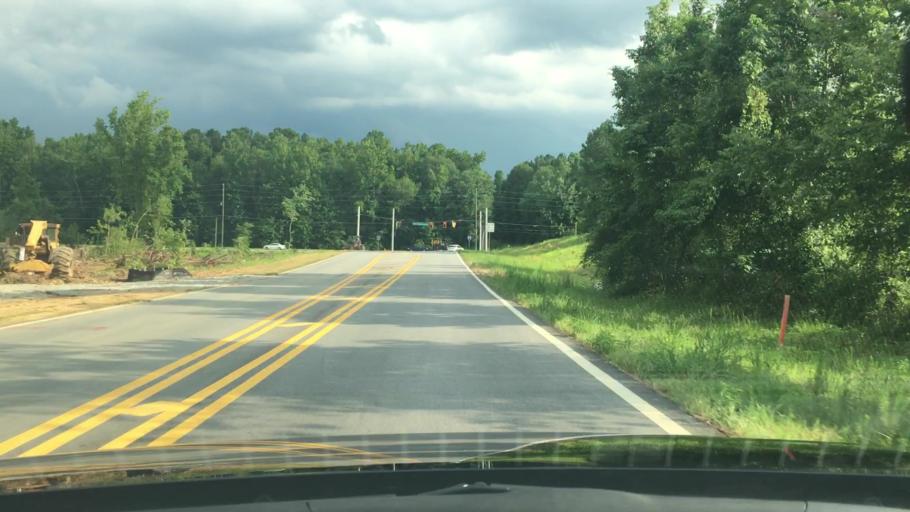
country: US
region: Georgia
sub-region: Coweta County
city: East Newnan
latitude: 33.3749
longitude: -84.7027
